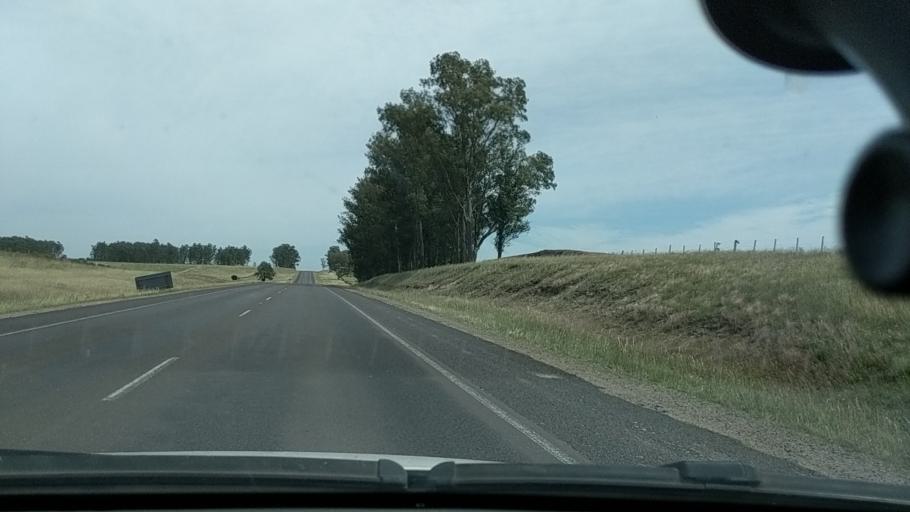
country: UY
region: Durazno
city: Durazno
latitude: -33.4662
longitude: -56.4583
